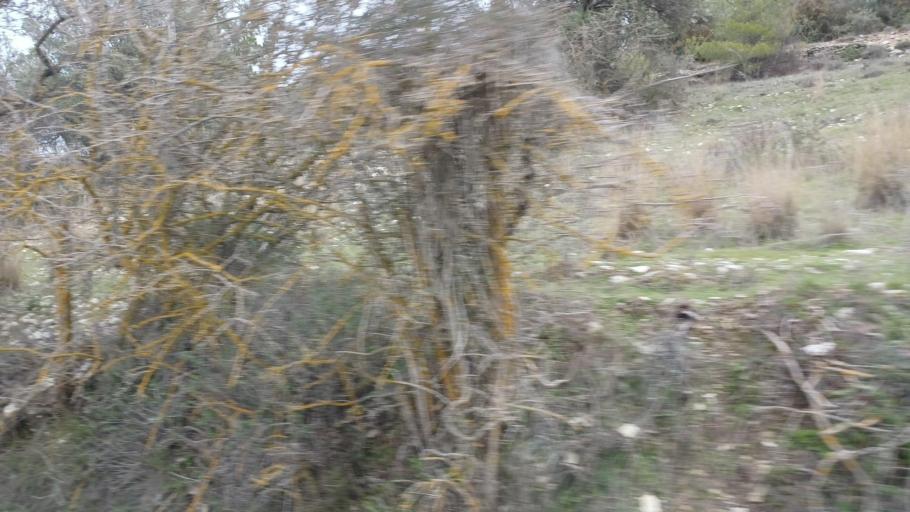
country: CY
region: Limassol
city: Pachna
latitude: 34.8463
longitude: 32.6784
